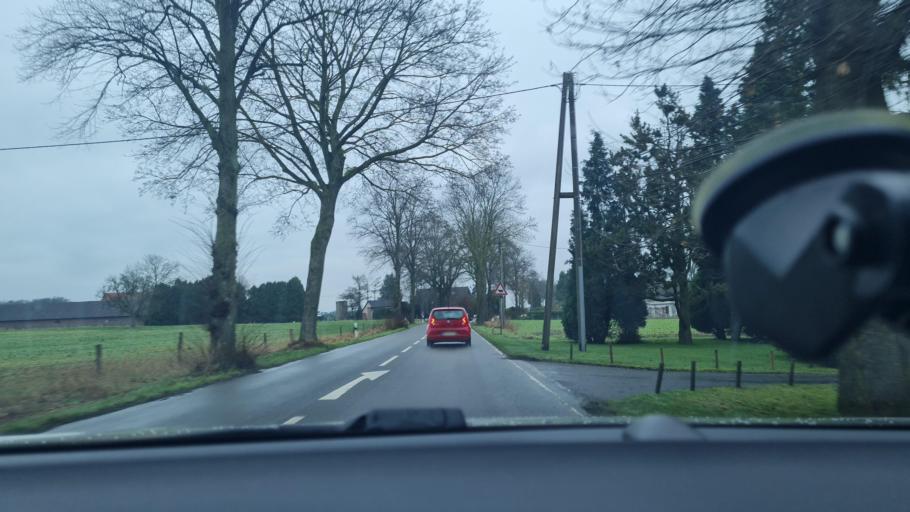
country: DE
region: North Rhine-Westphalia
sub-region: Regierungsbezirk Dusseldorf
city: Hunxe
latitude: 51.6834
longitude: 6.7433
